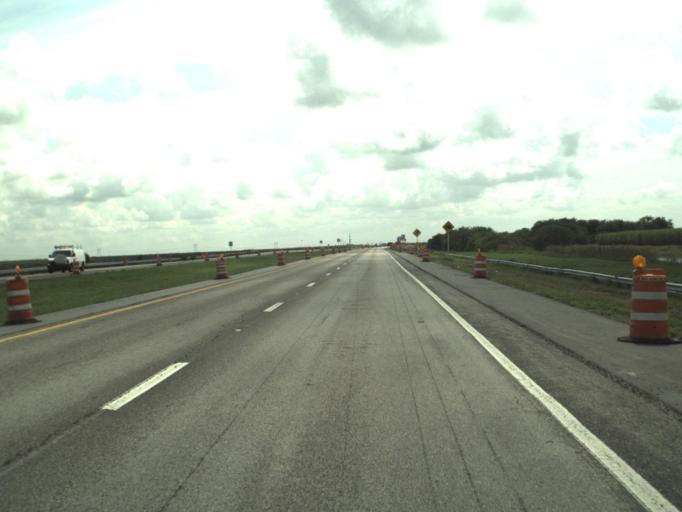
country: US
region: Florida
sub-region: Palm Beach County
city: Belle Glade
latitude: 26.7255
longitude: -80.4930
